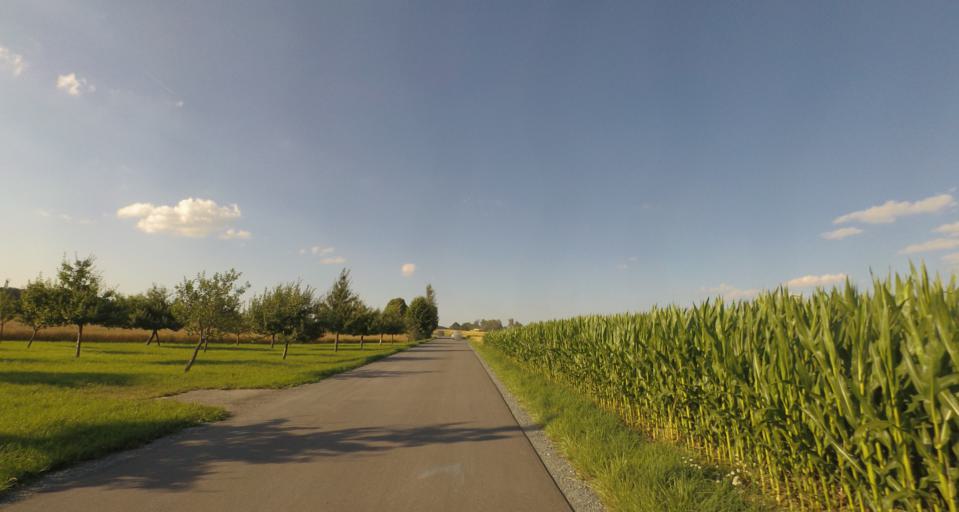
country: DE
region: Bavaria
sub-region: Upper Bavaria
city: Chieming
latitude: 47.9078
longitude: 12.5249
